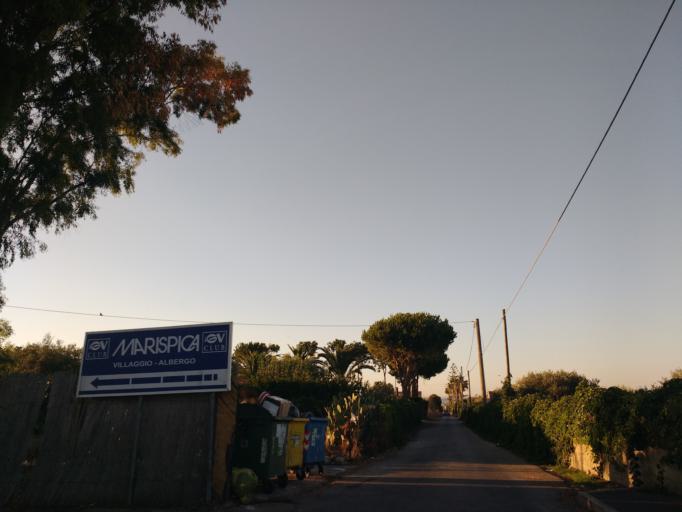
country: IT
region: Sicily
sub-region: Ragusa
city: Ispica
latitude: 36.7251
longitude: 14.9162
